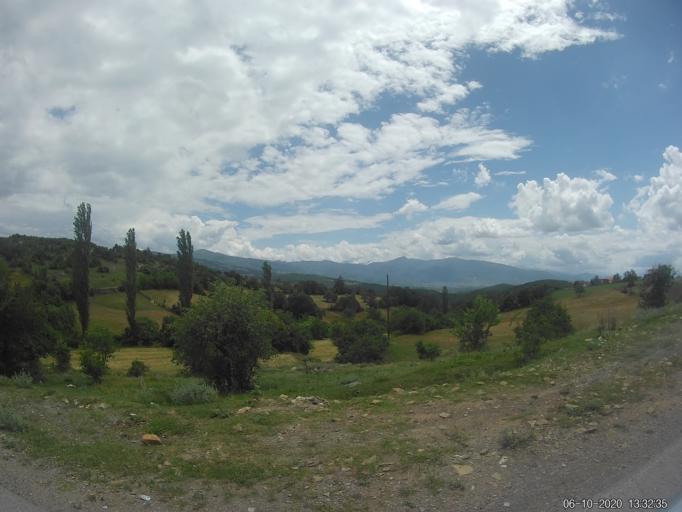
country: XK
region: Prizren
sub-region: Komuna e Therandes
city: Peqan
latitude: 42.4109
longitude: 20.8824
